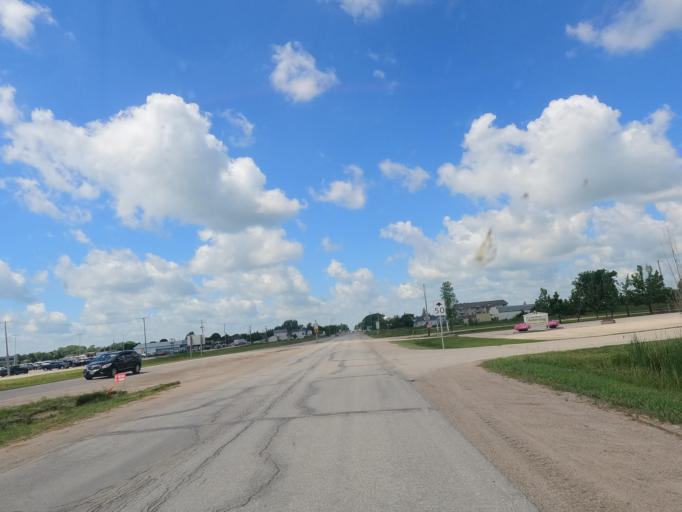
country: CA
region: Manitoba
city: Beausejour
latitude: 50.0618
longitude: -96.4998
